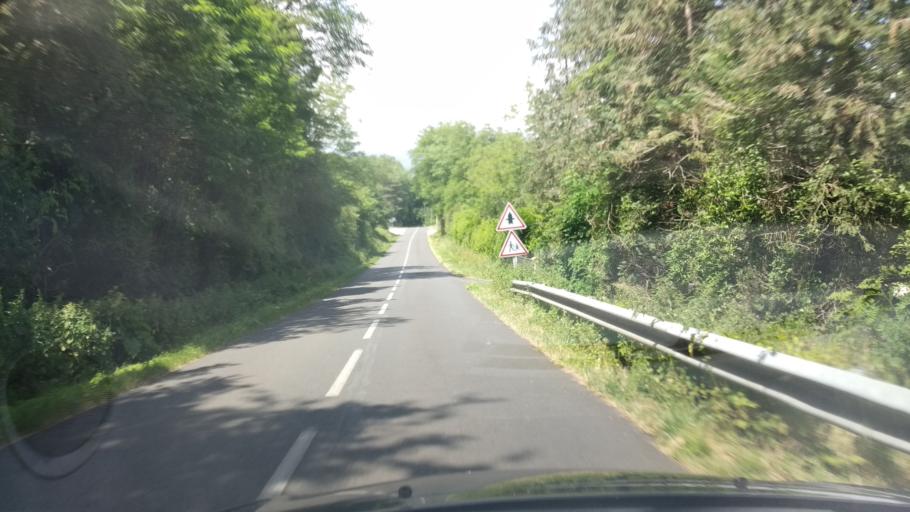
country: FR
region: Poitou-Charentes
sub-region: Departement de la Vienne
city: Cisse
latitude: 46.6147
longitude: 0.2210
